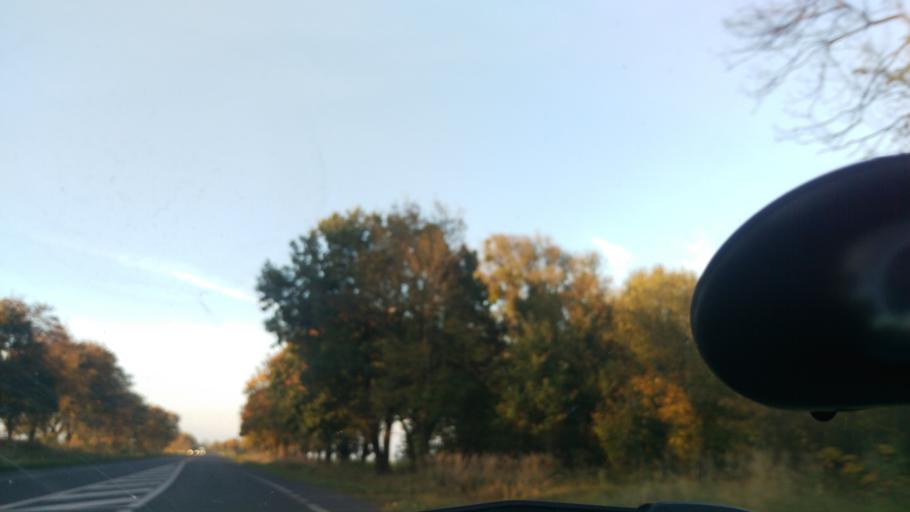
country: PL
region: West Pomeranian Voivodeship
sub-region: Powiat gryfinski
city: Stare Czarnowo
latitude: 53.2586
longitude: 14.7847
